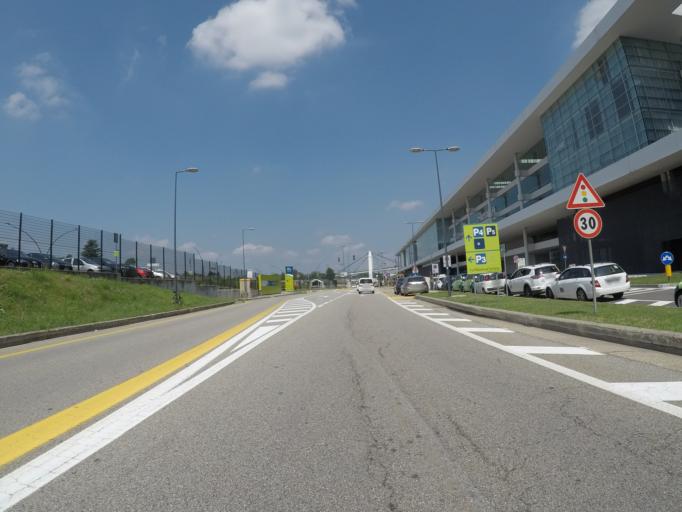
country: IT
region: Lombardy
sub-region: Provincia di Varese
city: Vizzola Ticino
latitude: 45.6262
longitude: 8.7107
